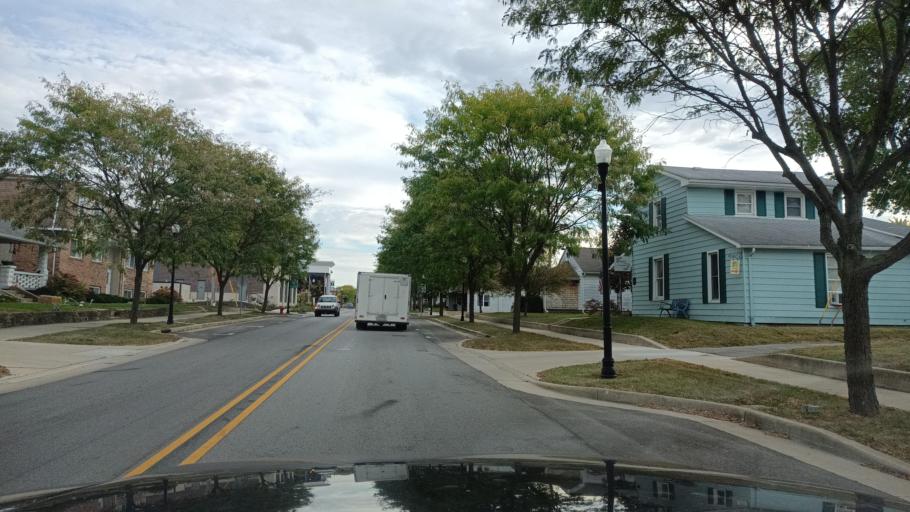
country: US
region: Indiana
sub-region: Delaware County
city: Yorktown
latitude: 40.1721
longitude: -85.4991
